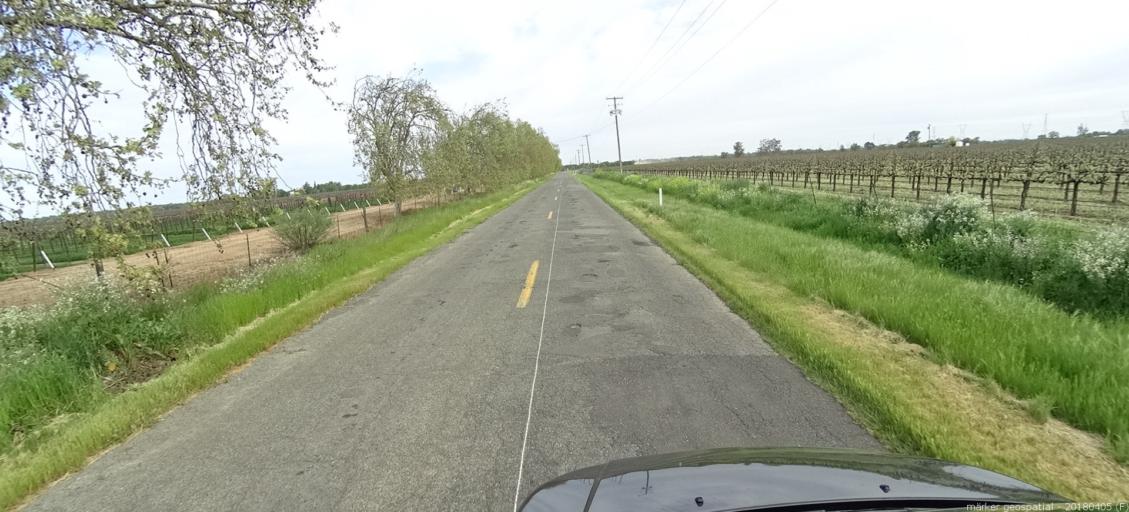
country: US
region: California
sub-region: San Joaquin County
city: Thornton
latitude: 38.2550
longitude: -121.3695
